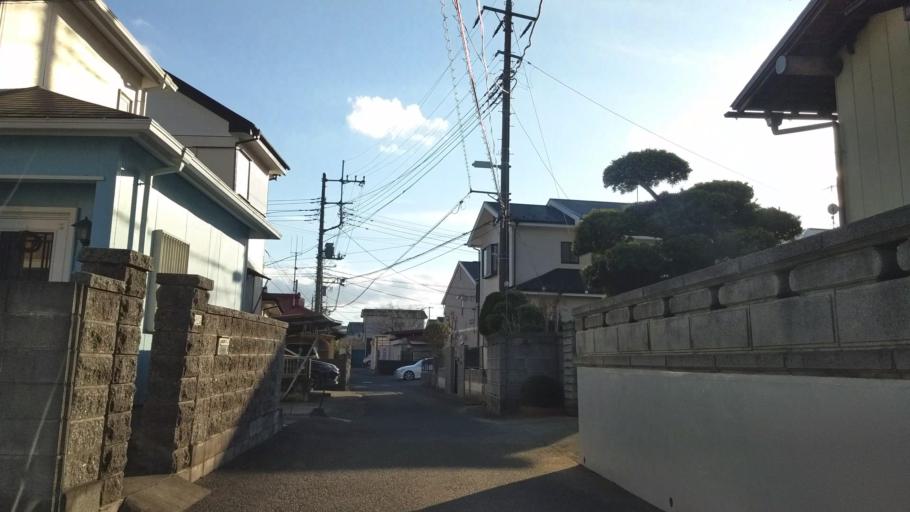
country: JP
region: Kanagawa
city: Isehara
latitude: 35.3584
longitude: 139.3057
